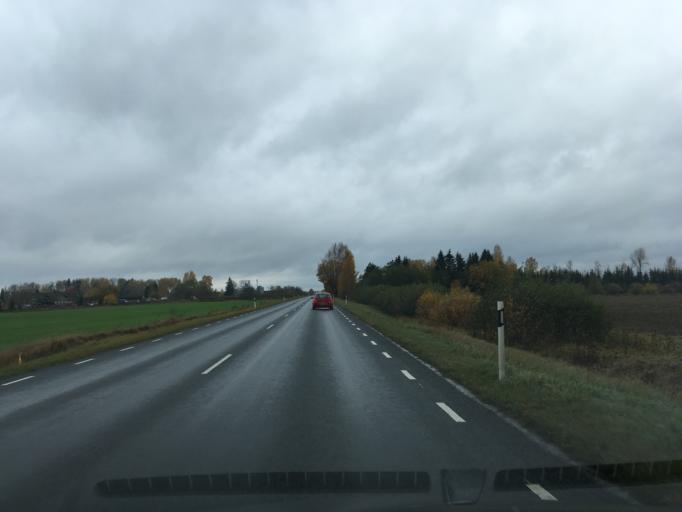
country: EE
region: Paernumaa
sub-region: Audru vald
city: Audru
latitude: 58.4487
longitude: 24.2324
